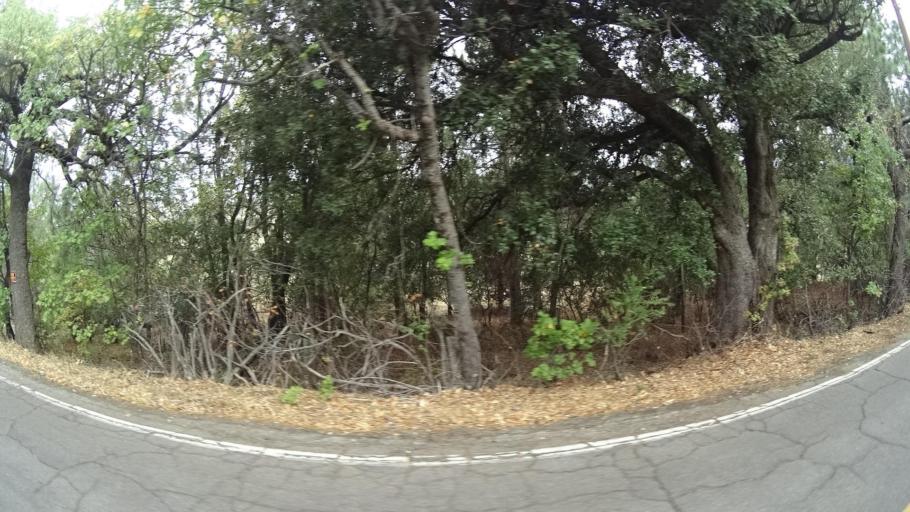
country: US
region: California
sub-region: San Diego County
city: Julian
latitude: 33.0425
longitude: -116.6000
